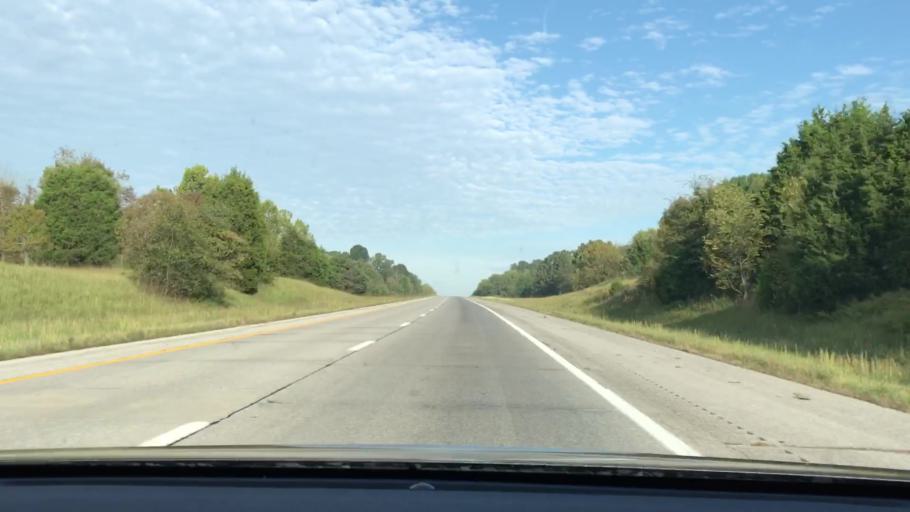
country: US
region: Kentucky
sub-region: Trigg County
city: Cadiz
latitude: 36.9513
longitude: -87.8427
